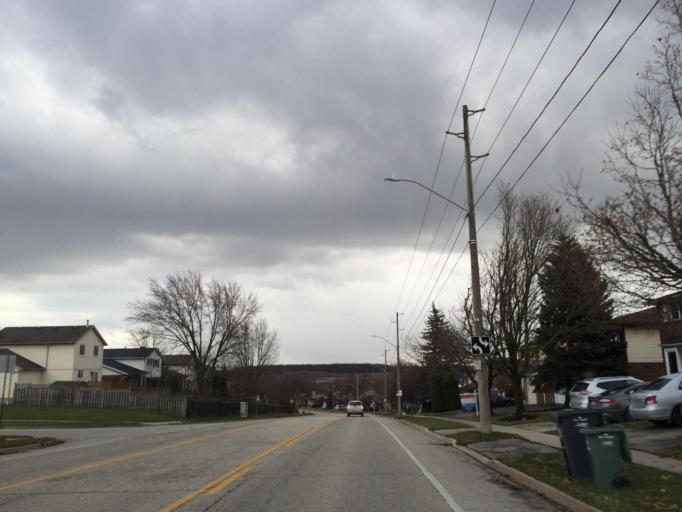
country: CA
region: Ontario
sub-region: Wellington County
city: Guelph
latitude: 43.5322
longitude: -80.2944
